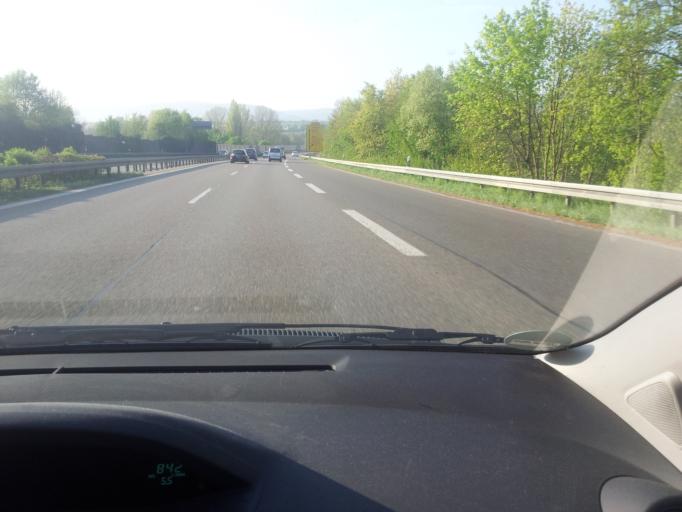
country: DE
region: Baden-Wuerttemberg
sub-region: Regierungsbezirk Stuttgart
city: Waiblingen
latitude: 48.8271
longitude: 9.3331
